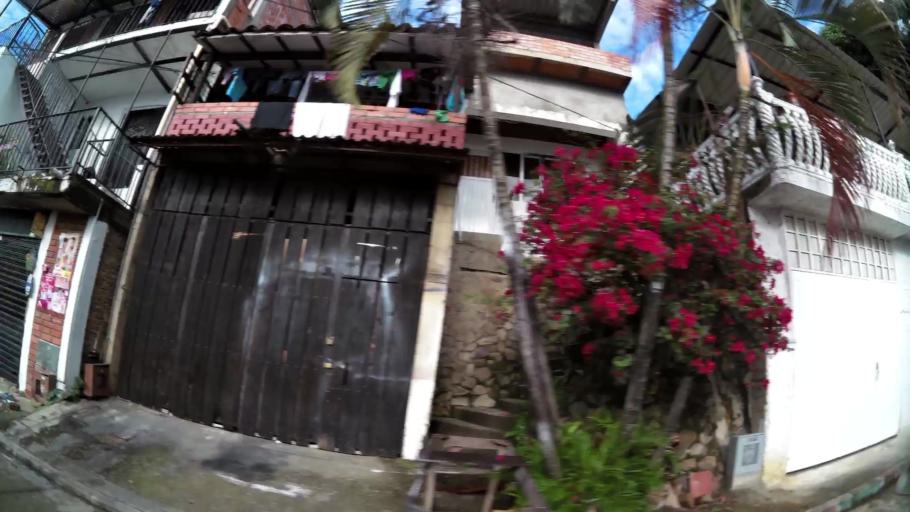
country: CO
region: Valle del Cauca
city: Cali
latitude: 3.4424
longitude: -76.5501
